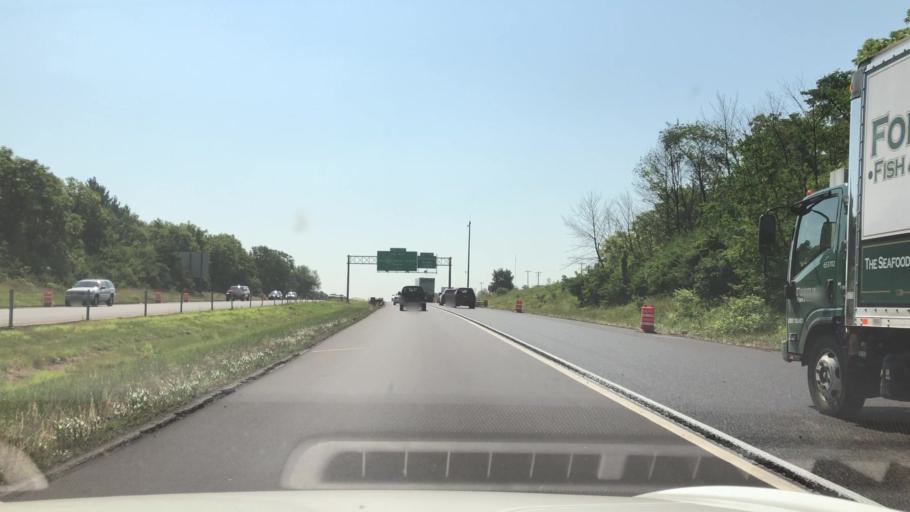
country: US
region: Illinois
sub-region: Tazewell County
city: East Peoria
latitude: 40.6493
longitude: -89.5554
